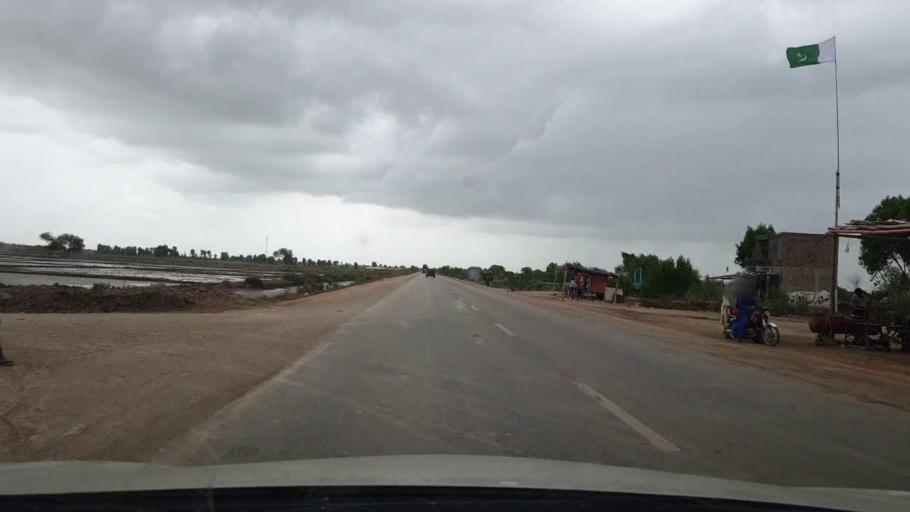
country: PK
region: Sindh
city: Kario
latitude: 24.6431
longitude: 68.4700
